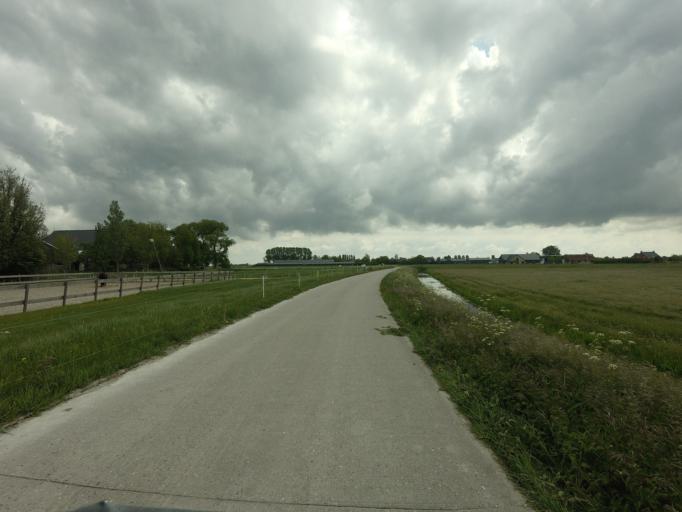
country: NL
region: Friesland
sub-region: Gemeente Littenseradiel
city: Wommels
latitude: 53.1065
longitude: 5.6219
